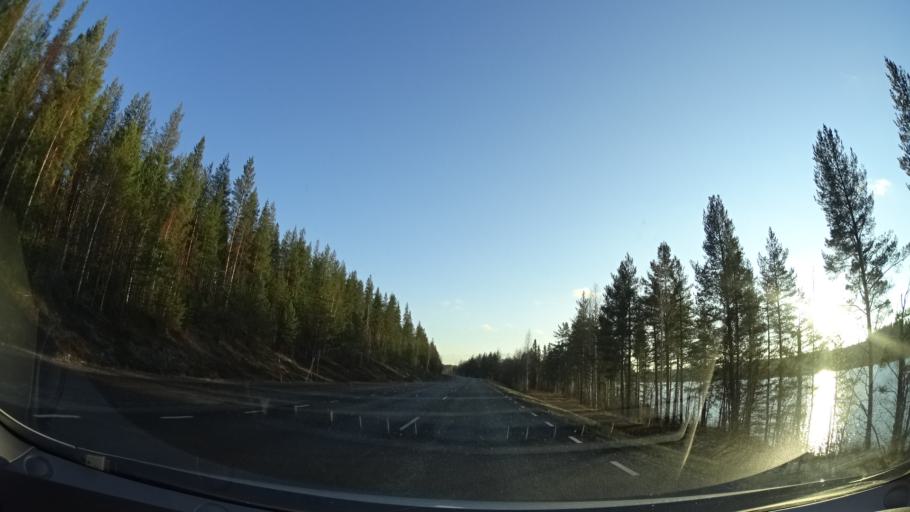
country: SE
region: Vaesterbotten
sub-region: Lycksele Kommun
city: Lycksele
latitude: 64.6273
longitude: 18.6819
